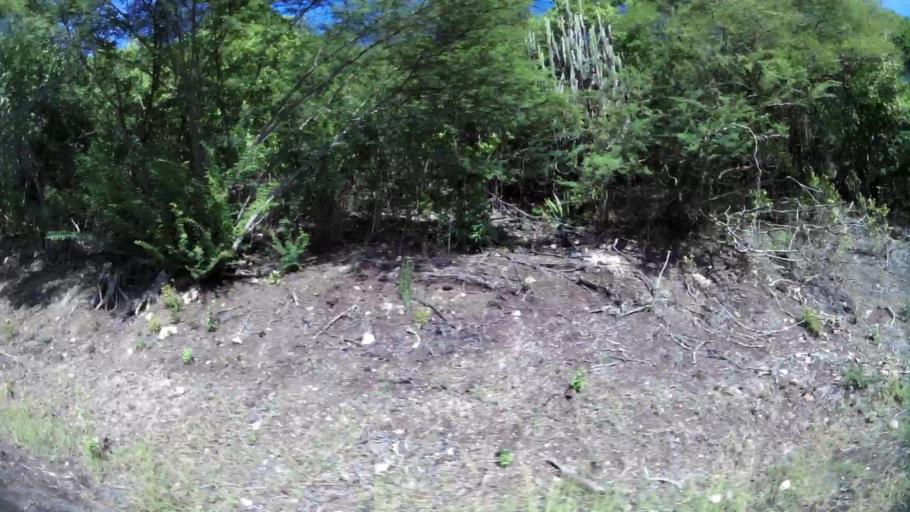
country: AG
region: Saint Paul
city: Falmouth
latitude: 17.0218
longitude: -61.7426
